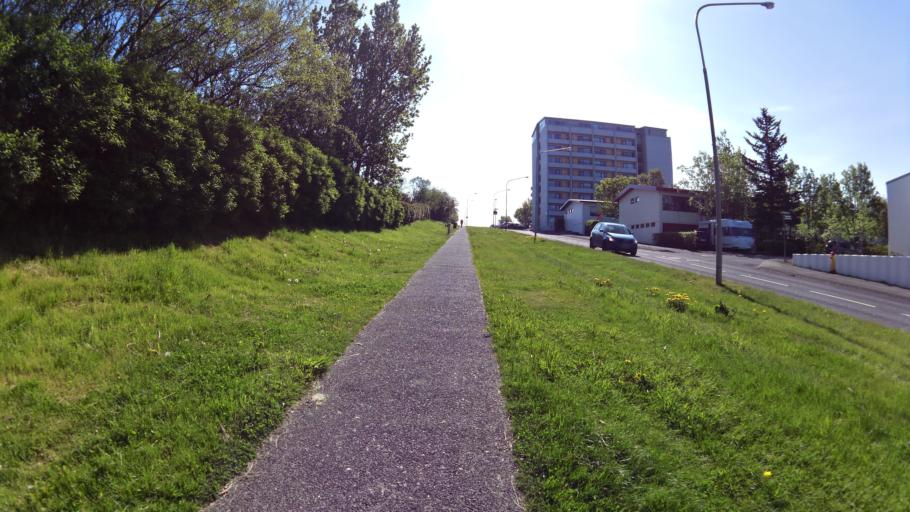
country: IS
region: Capital Region
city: Reykjavik
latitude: 64.1255
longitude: -21.8849
